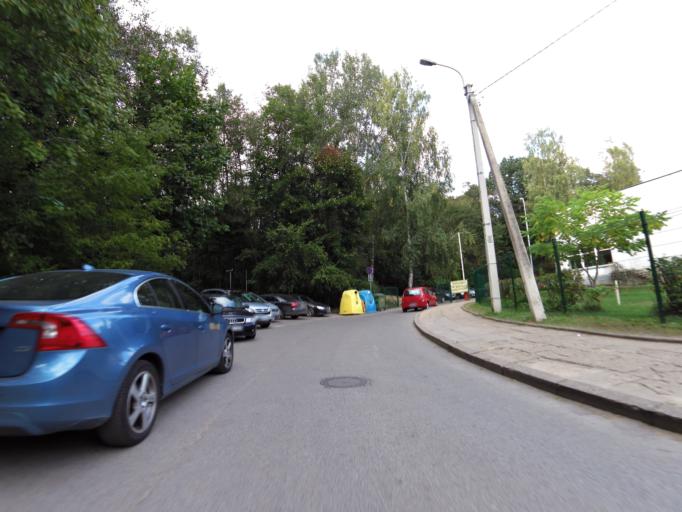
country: LT
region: Vilnius County
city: Seskine
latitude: 54.7050
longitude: 25.2489
